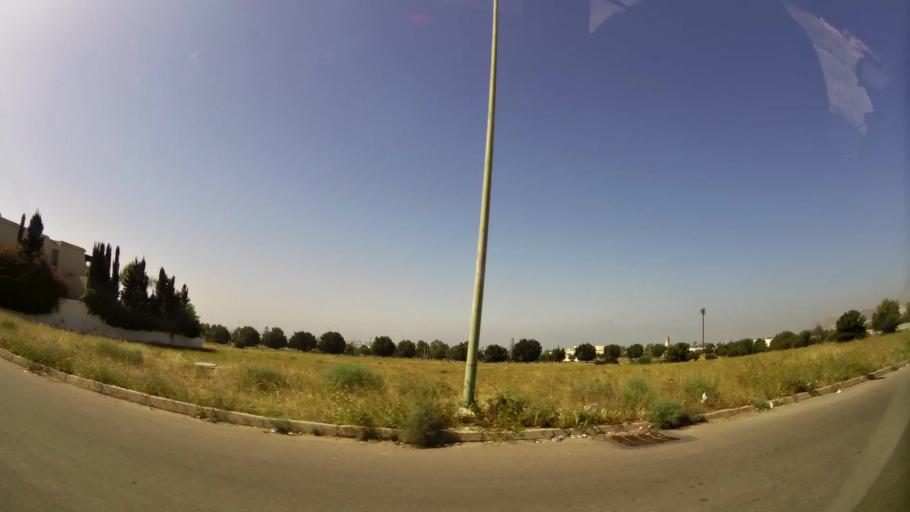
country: MA
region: Souss-Massa-Draa
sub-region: Agadir-Ida-ou-Tnan
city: Agadir
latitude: 30.4388
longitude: -9.5824
